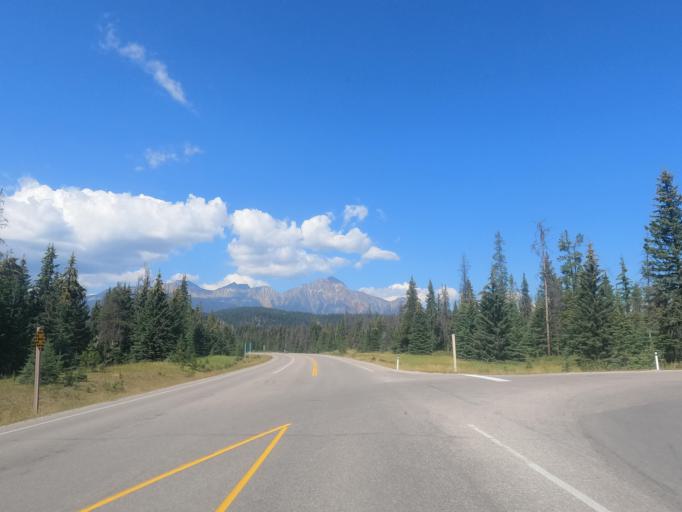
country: CA
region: Alberta
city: Jasper Park Lodge
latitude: 52.8583
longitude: -118.0794
